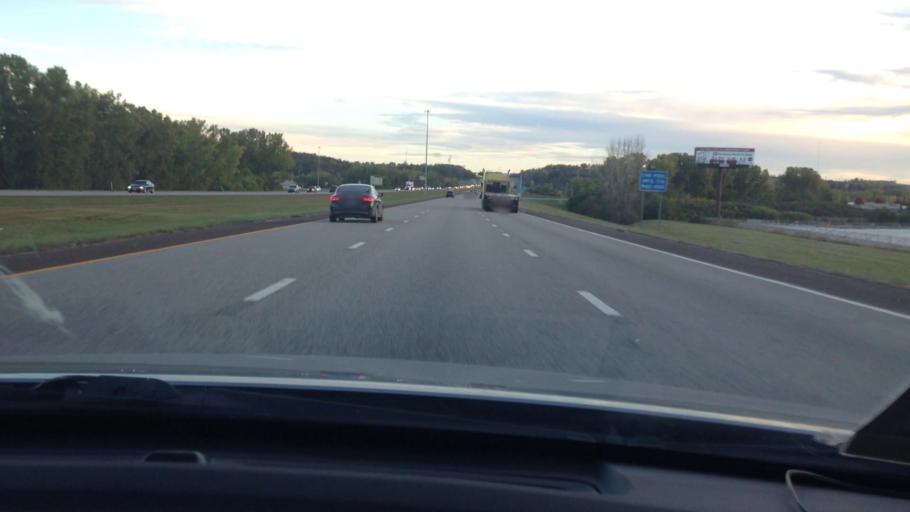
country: US
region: Kansas
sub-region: Wyandotte County
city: Edwardsville
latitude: 39.0572
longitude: -94.7911
